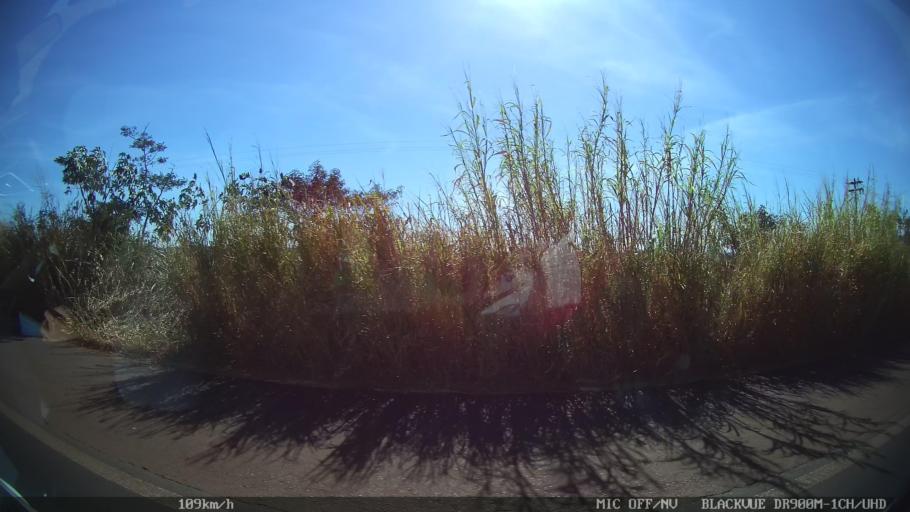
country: BR
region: Sao Paulo
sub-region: Barretos
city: Barretos
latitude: -20.4798
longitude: -48.5022
